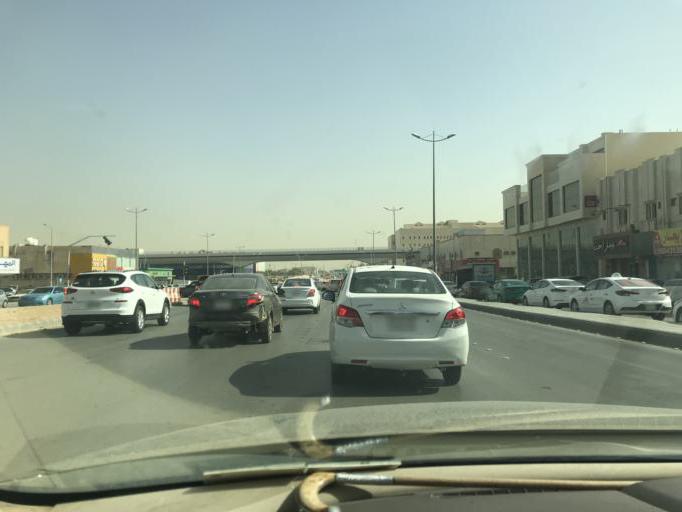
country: SA
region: Ar Riyad
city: Riyadh
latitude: 24.7947
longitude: 46.7429
